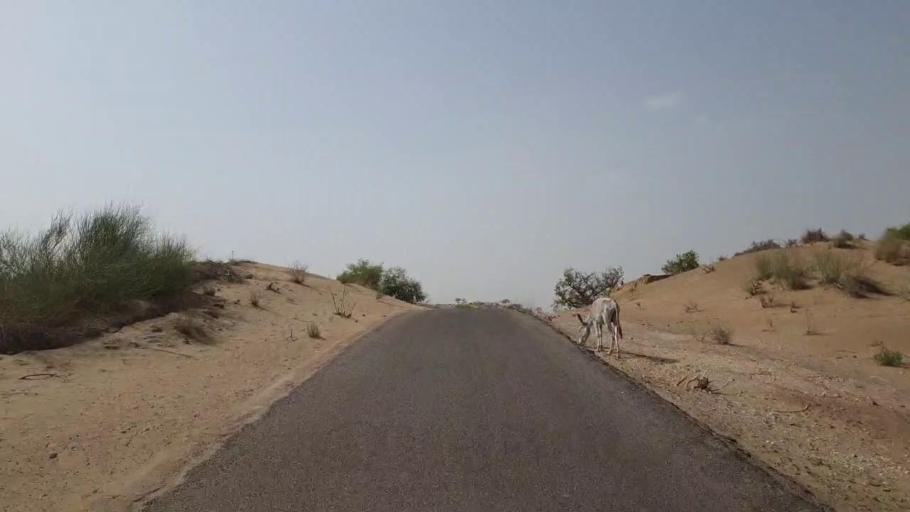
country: PK
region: Sindh
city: Mithi
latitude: 24.5826
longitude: 69.9229
